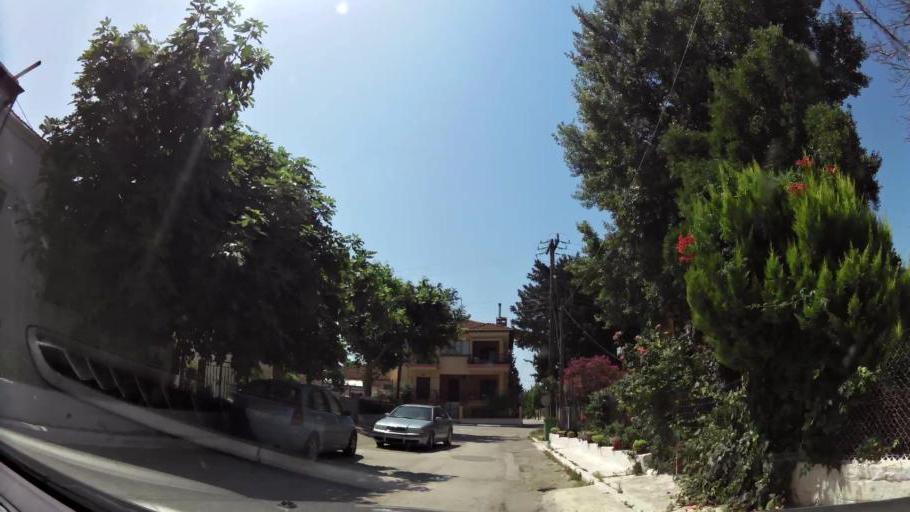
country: GR
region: Central Macedonia
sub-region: Nomos Thessalonikis
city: Agia Triada
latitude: 40.4959
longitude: 22.8323
